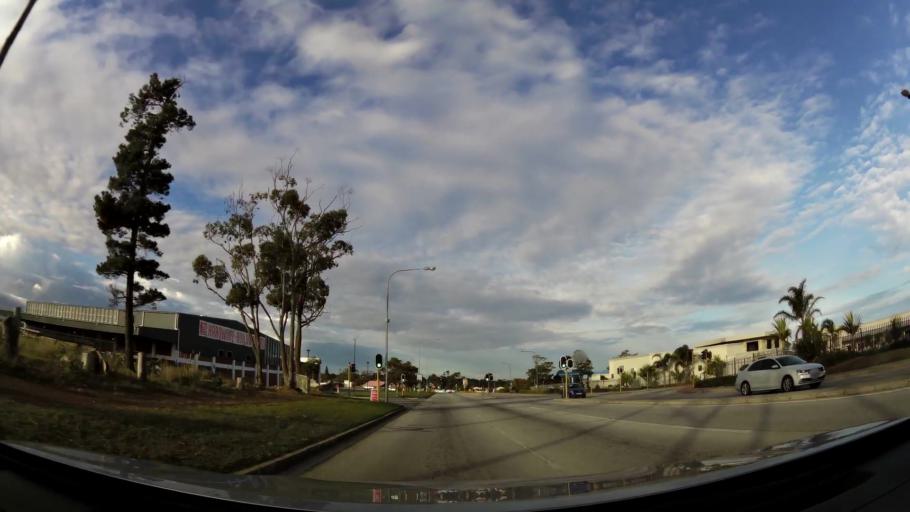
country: ZA
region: Eastern Cape
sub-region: Nelson Mandela Bay Metropolitan Municipality
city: Port Elizabeth
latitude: -33.9572
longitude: 25.5028
